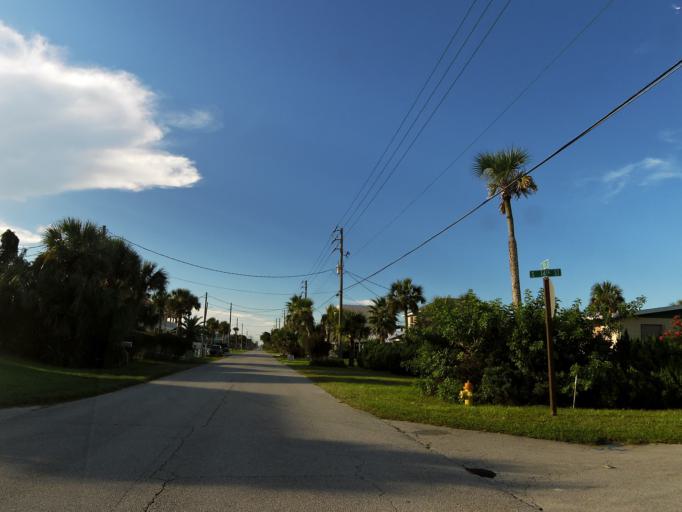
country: US
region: Florida
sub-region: Flagler County
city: Flagler Beach
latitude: 29.4702
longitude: -81.1233
